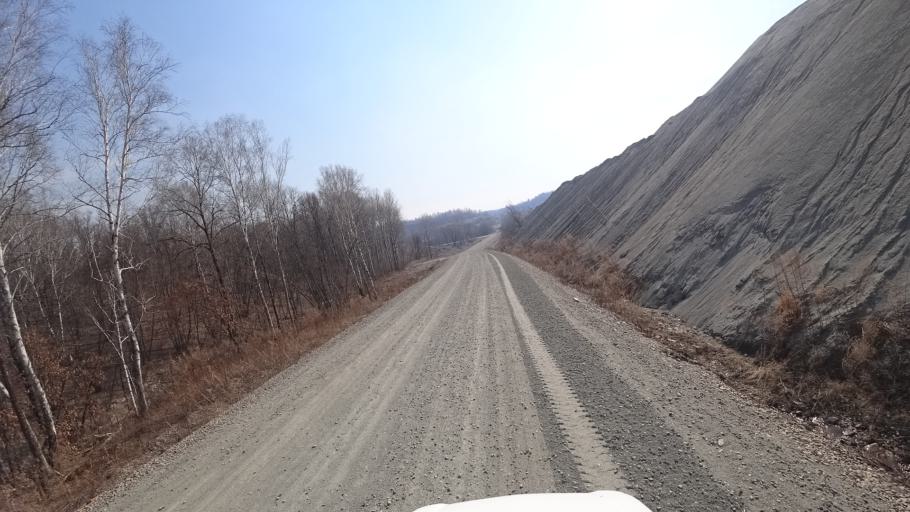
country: RU
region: Amur
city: Novobureyskiy
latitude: 49.7992
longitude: 129.9585
